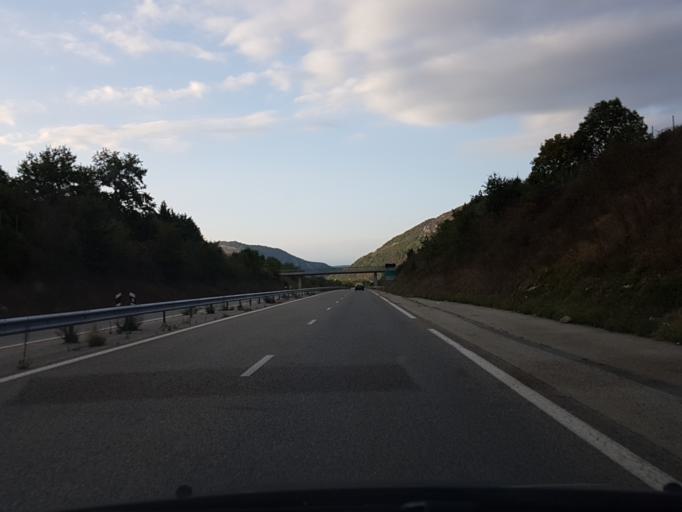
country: FR
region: Midi-Pyrenees
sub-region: Departement de l'Ariege
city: Montgaillard
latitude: 42.9364
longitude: 1.6258
